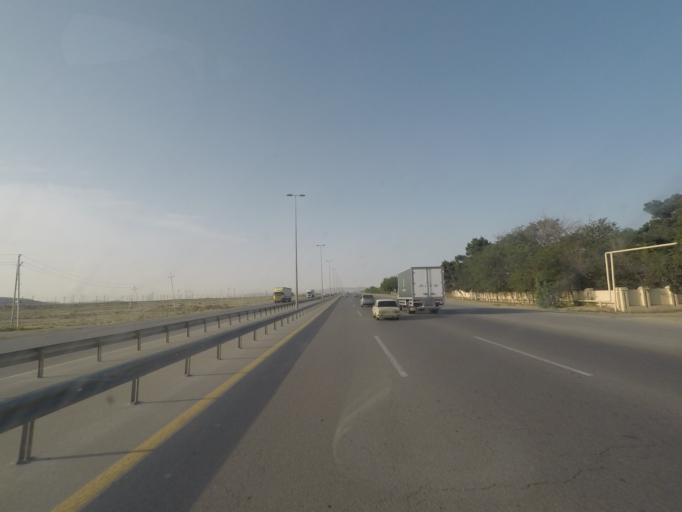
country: AZ
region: Baki
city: Qobustan
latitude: 40.0997
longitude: 49.4234
